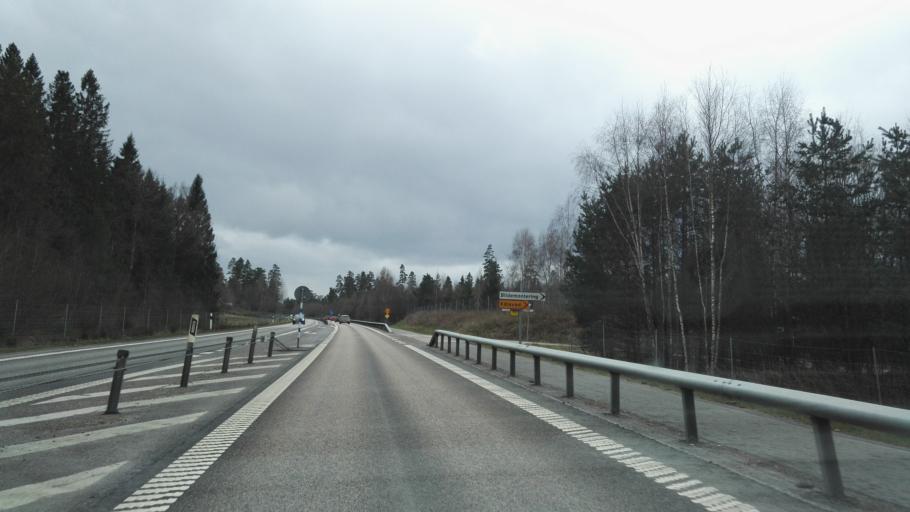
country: SE
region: Skane
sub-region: Osby Kommun
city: Osby
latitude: 56.4024
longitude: 14.0393
